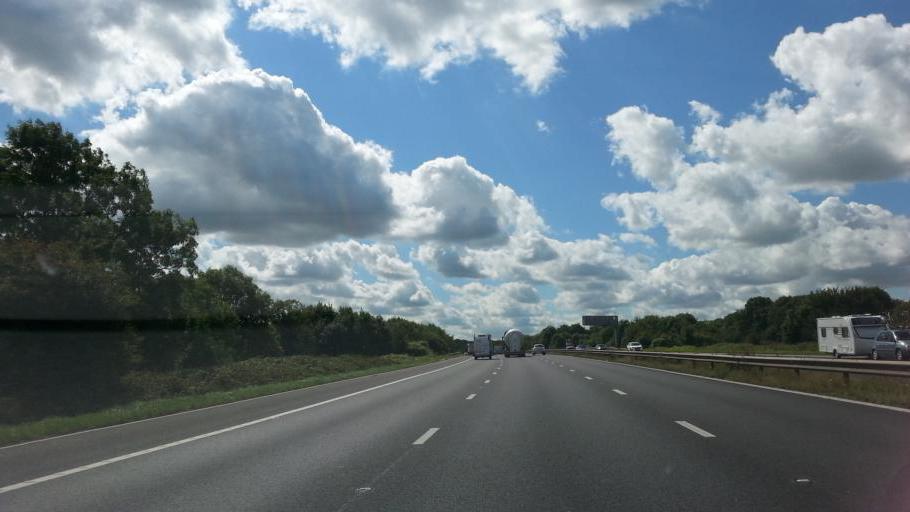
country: GB
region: England
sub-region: Leicestershire
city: Cosby
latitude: 52.5501
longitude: -1.1858
